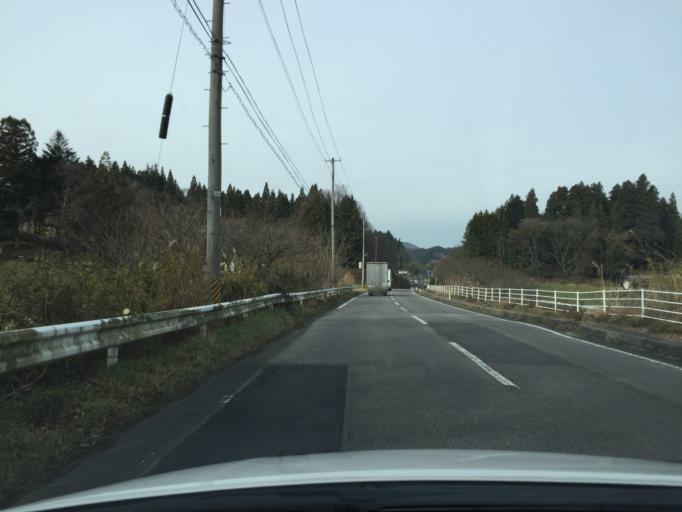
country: JP
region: Fukushima
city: Funehikimachi-funehiki
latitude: 37.2764
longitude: 140.6260
